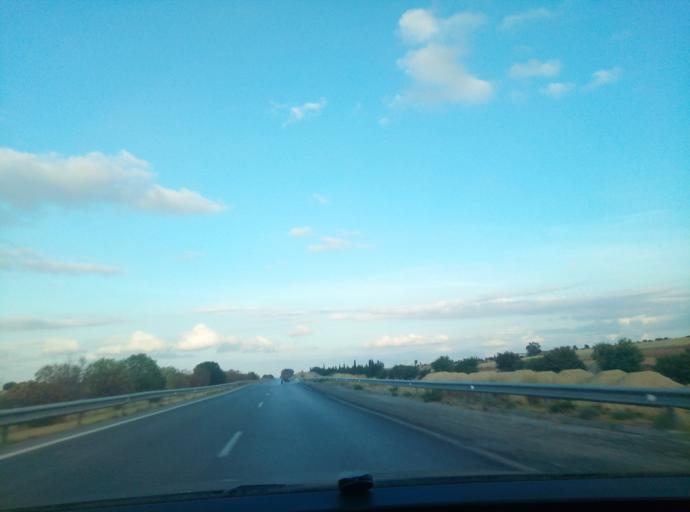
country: TN
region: Manouba
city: El Battan
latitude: 36.6598
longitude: 9.8141
